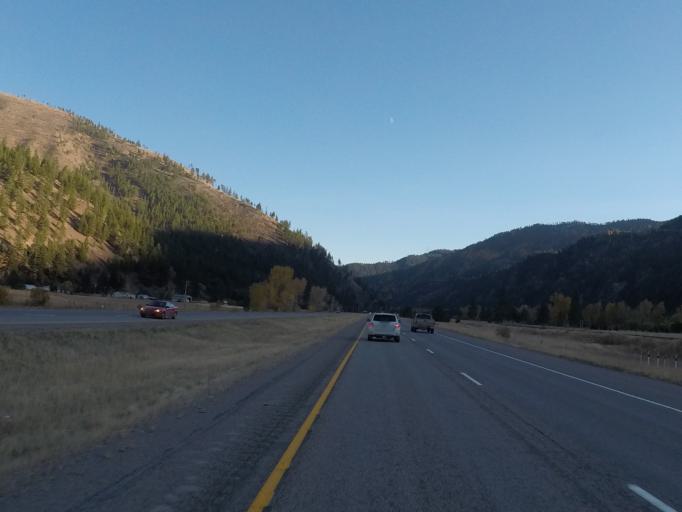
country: US
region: Montana
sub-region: Missoula County
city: Clinton
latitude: 46.7430
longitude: -113.7022
